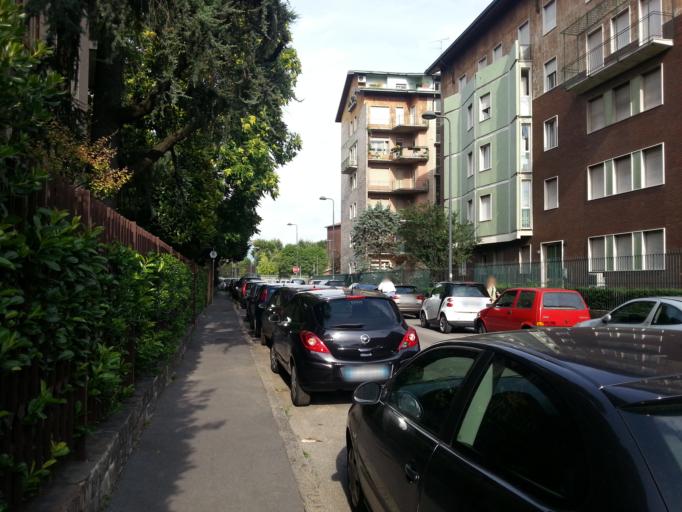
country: IT
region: Lombardy
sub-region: Citta metropolitana di Milano
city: Milano
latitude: 45.4975
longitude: 9.1986
